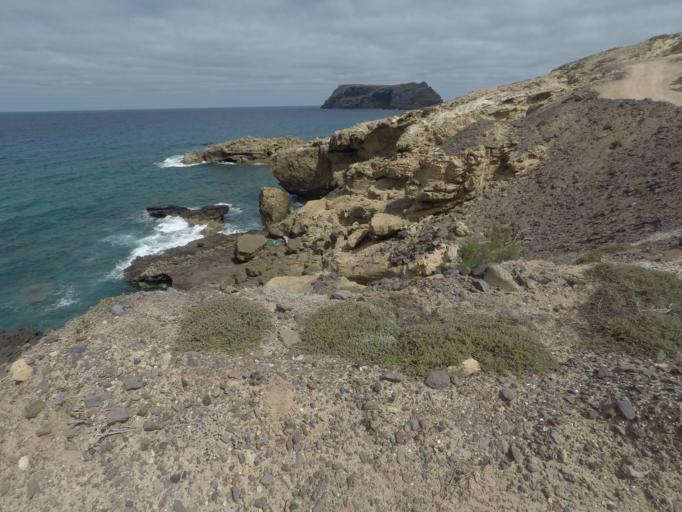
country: PT
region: Madeira
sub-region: Porto Santo
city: Vila de Porto Santo
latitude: 33.0655
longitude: -16.2968
